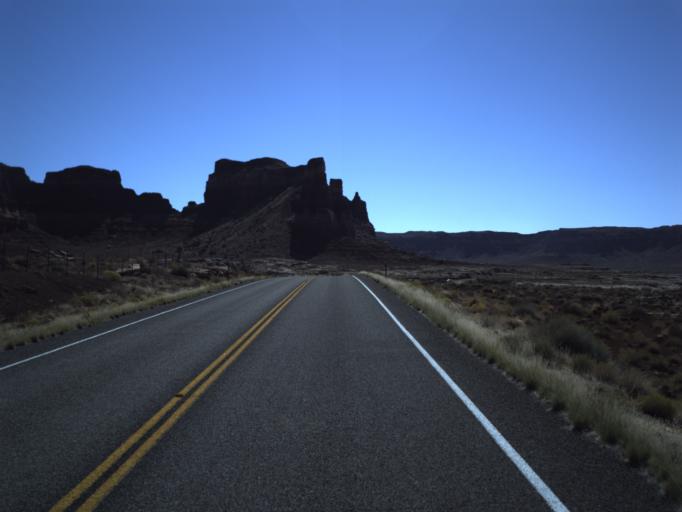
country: US
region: Utah
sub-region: San Juan County
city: Blanding
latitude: 37.9077
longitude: -110.3829
